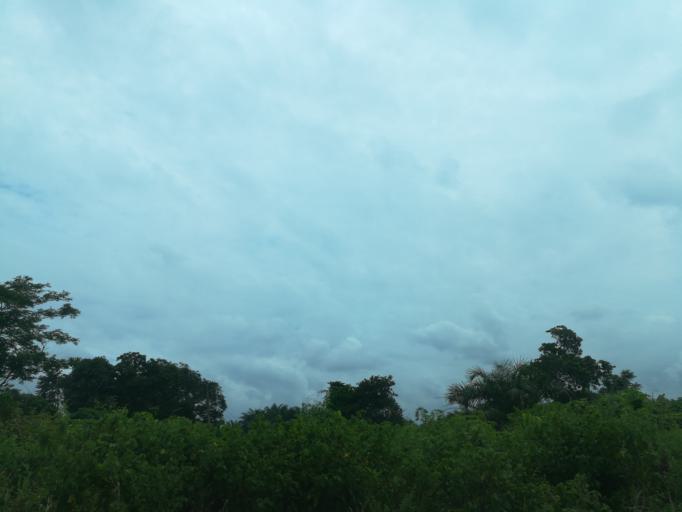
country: NG
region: Lagos
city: Ejirin
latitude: 6.6481
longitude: 3.8315
